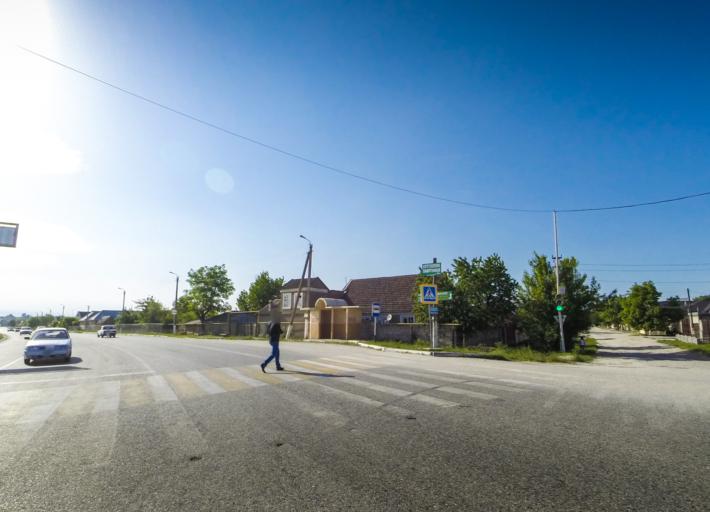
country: RU
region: Kabardino-Balkariya
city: Urvan'
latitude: 43.4965
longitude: 43.7640
